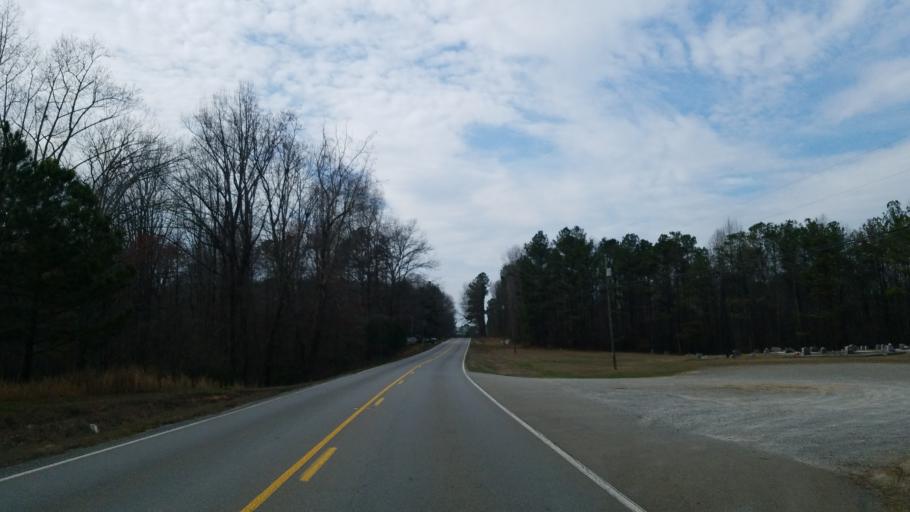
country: US
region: Georgia
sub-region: Cherokee County
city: Ball Ground
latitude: 34.3065
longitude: -84.3322
